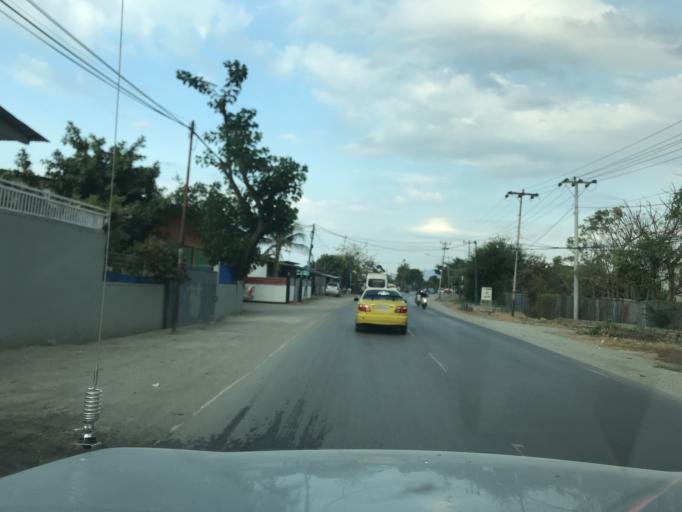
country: TL
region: Dili
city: Dili
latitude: -8.5531
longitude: 125.5210
